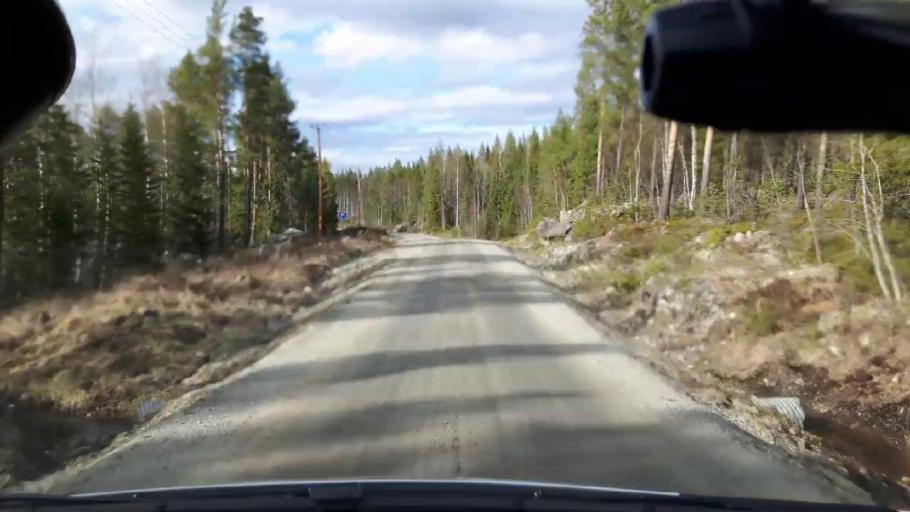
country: SE
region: Jaemtland
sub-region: Bergs Kommun
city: Hoverberg
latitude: 62.8722
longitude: 14.6660
